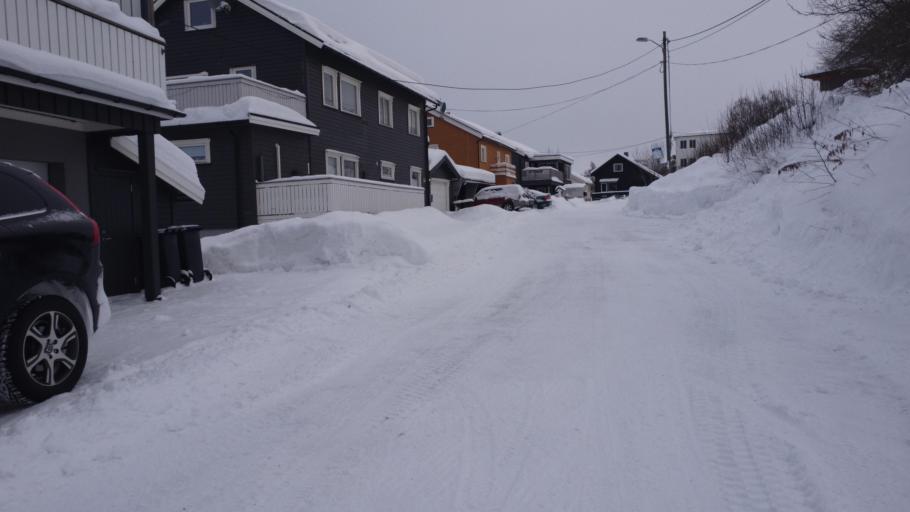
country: NO
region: Nordland
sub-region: Rana
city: Mo i Rana
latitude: 66.3157
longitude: 14.1439
